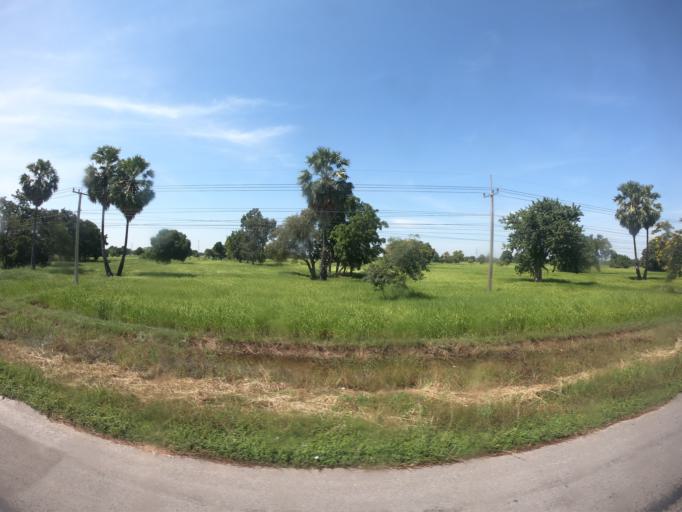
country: TH
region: Nakhon Ratchasima
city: Bua Lai
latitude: 15.6302
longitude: 102.5677
